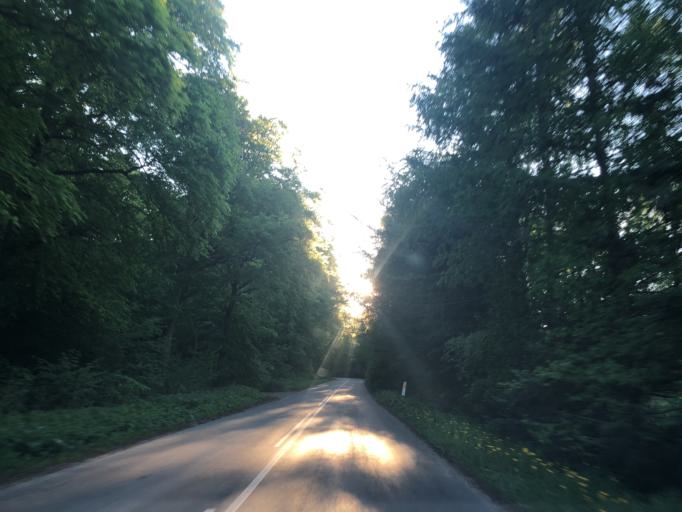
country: DK
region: Zealand
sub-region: Koge Kommune
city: Bjaeverskov
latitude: 55.4262
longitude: 12.0777
